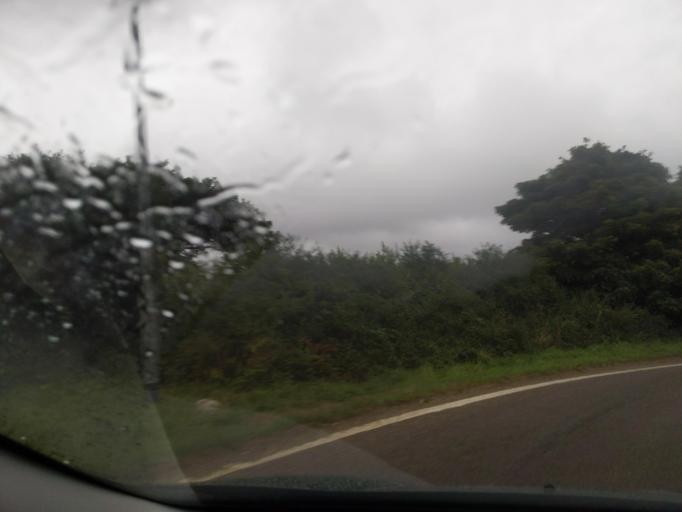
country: GB
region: England
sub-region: Cornwall
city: Camborne
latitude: 50.2186
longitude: -5.3198
